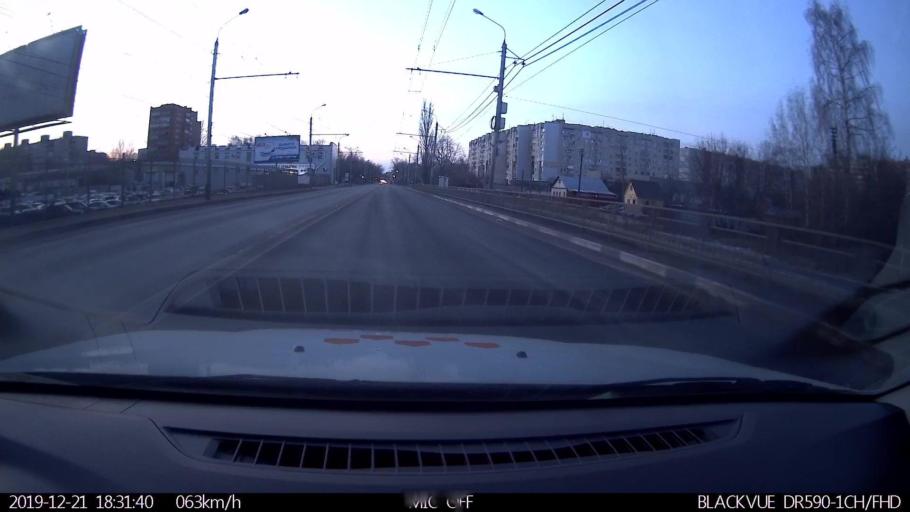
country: RU
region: Nizjnij Novgorod
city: Nizhniy Novgorod
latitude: 56.3330
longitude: 43.9183
